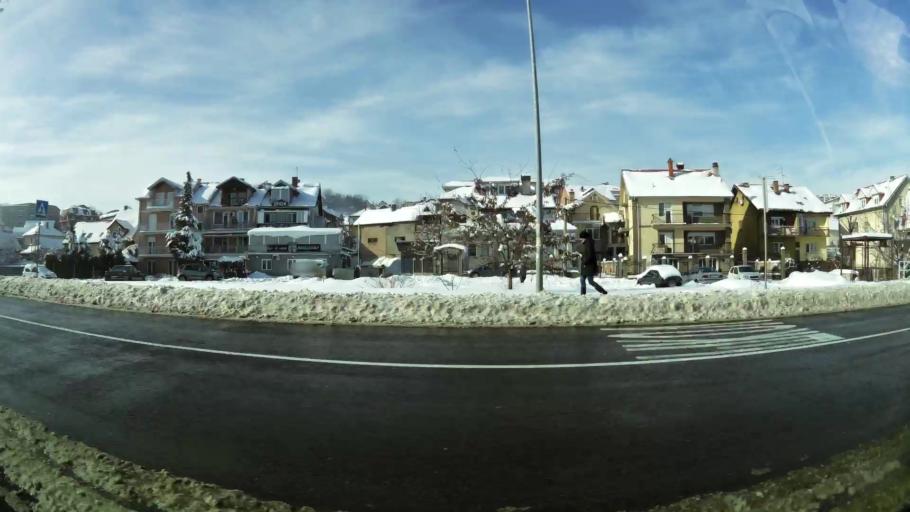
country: RS
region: Central Serbia
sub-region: Belgrade
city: Palilula
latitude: 44.7959
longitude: 20.5272
